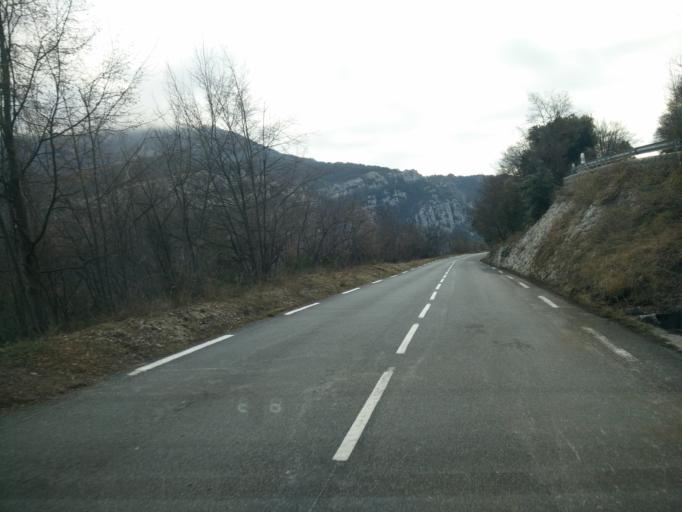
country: FR
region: Provence-Alpes-Cote d'Azur
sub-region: Departement des Alpes-Maritimes
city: Tourrettes-sur-Loup
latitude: 43.7397
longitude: 6.9931
